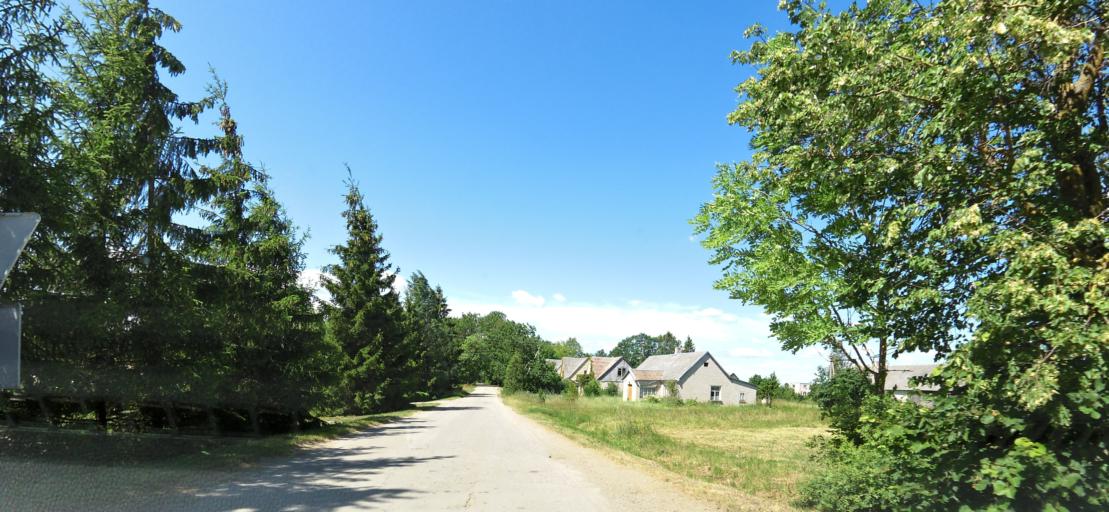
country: LT
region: Panevezys
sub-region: Birzai
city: Birzai
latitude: 56.2536
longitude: 24.5470
